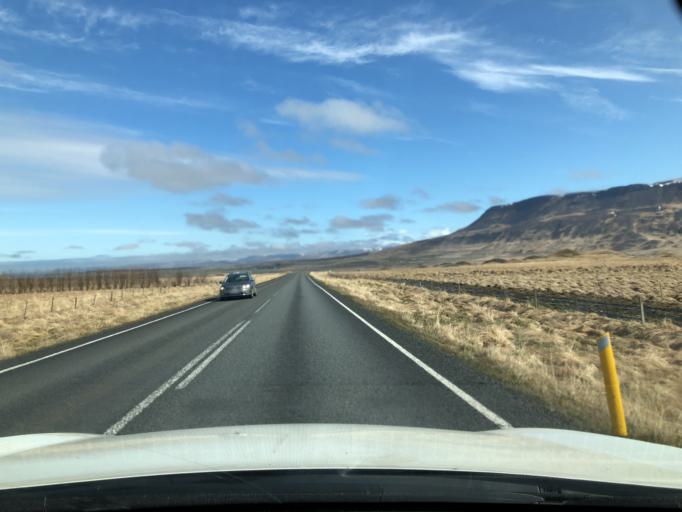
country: IS
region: Northwest
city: Saudarkrokur
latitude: 65.4973
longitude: -20.4050
